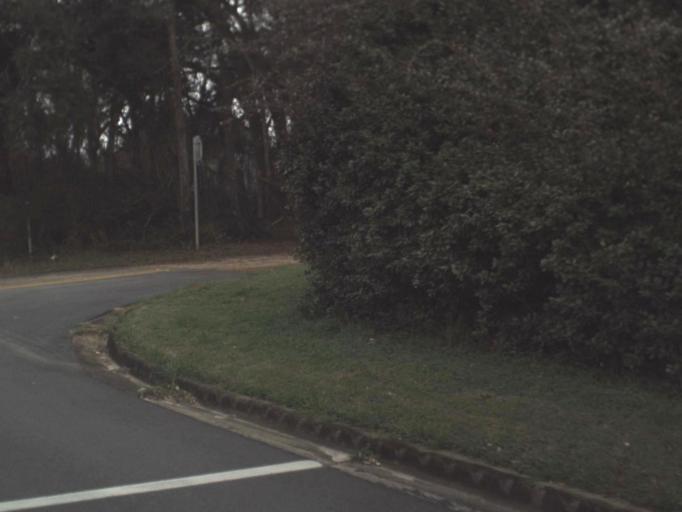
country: US
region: Florida
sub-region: Jefferson County
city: Monticello
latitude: 30.4117
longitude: -83.9505
